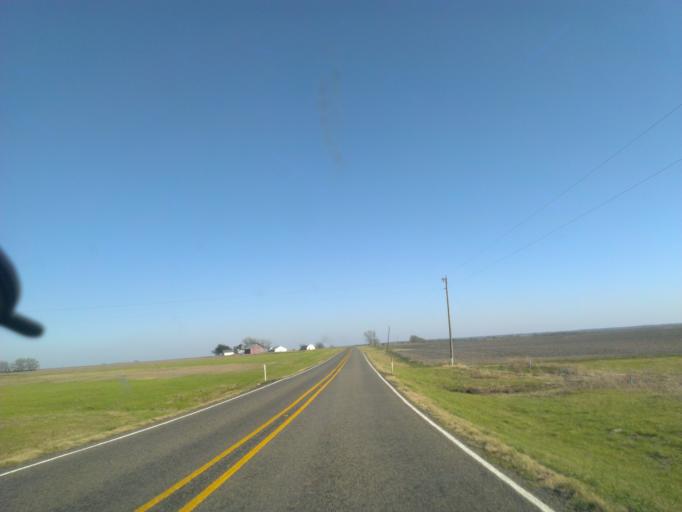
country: US
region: Texas
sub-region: Milam County
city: Thorndale
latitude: 30.5527
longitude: -97.2917
